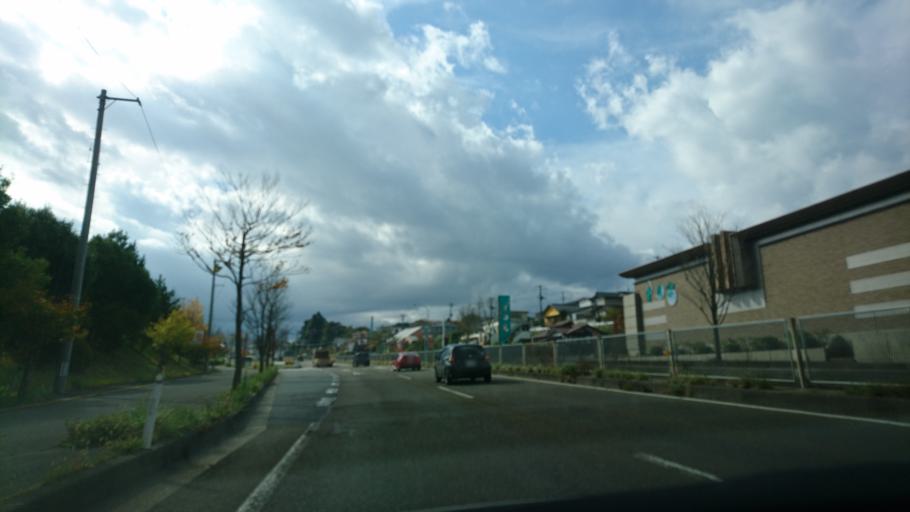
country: JP
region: Miyagi
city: Tomiya
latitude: 38.3661
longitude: 140.8730
